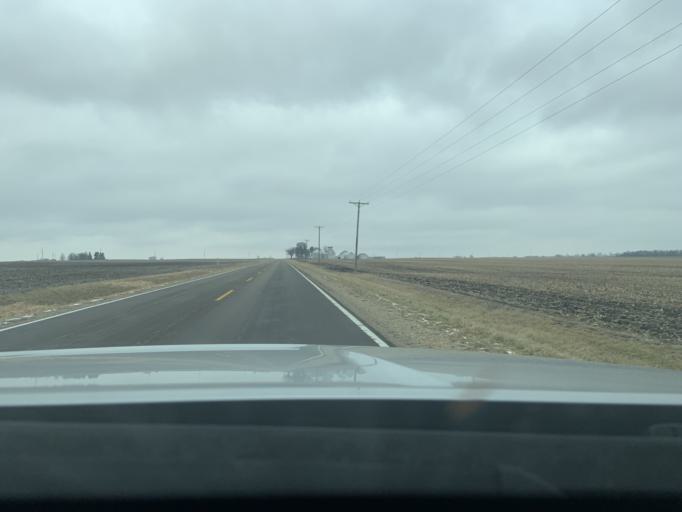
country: US
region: Illinois
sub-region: LaSalle County
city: Sheridan
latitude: 41.4508
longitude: -88.6152
